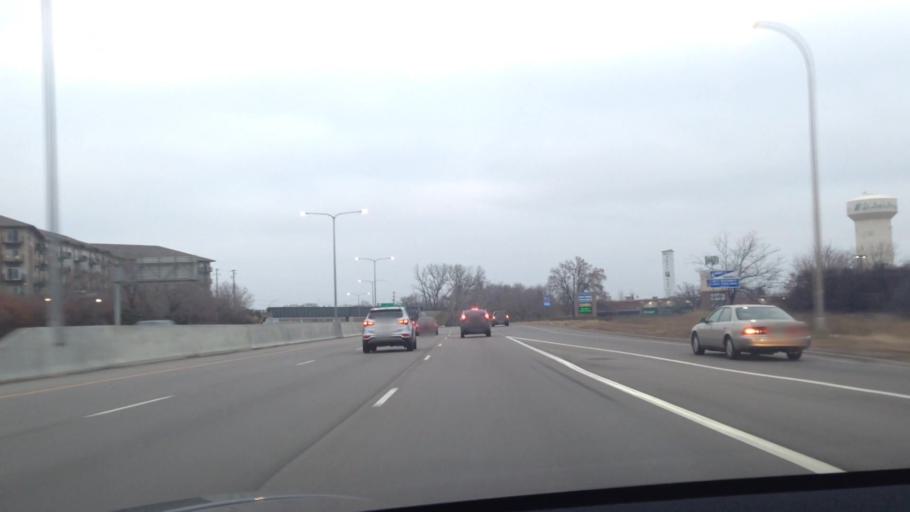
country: US
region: Minnesota
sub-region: Hennepin County
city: Saint Louis Park
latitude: 44.9380
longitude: -93.3490
